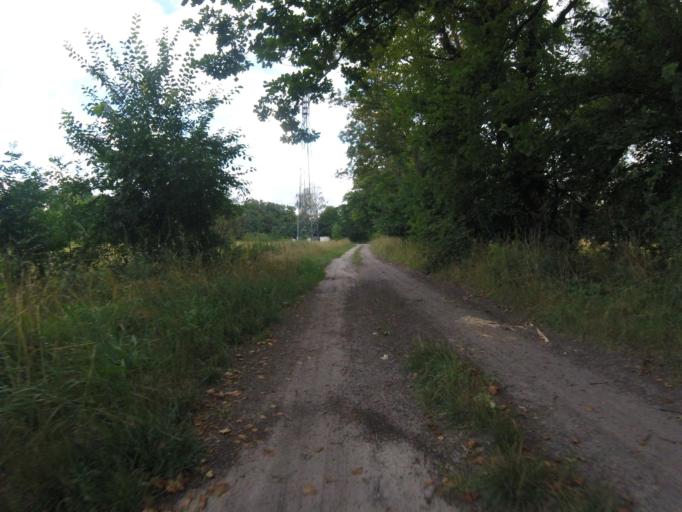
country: DE
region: Brandenburg
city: Mittenwalde
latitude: 52.2918
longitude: 13.5501
